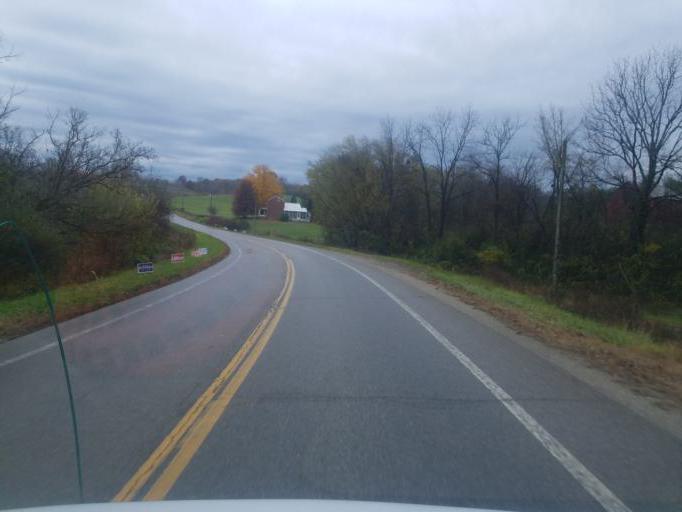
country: US
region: Ohio
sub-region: Morgan County
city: McConnelsville
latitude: 39.5022
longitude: -81.8558
